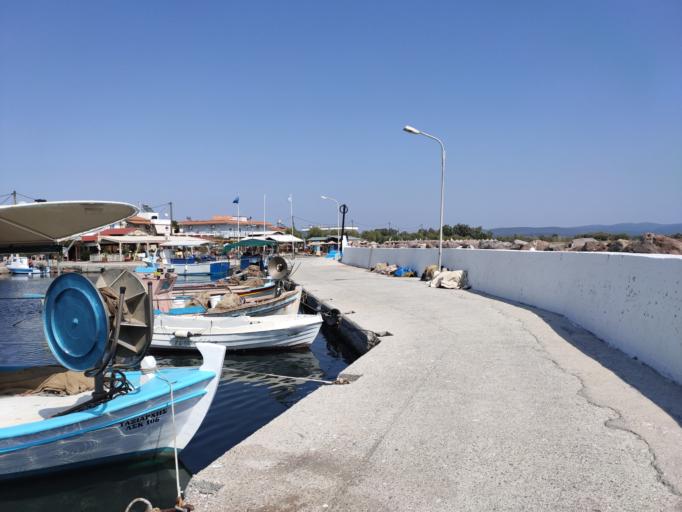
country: GR
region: North Aegean
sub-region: Nomos Lesvou
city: Kalloni
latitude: 39.2051
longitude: 26.2102
